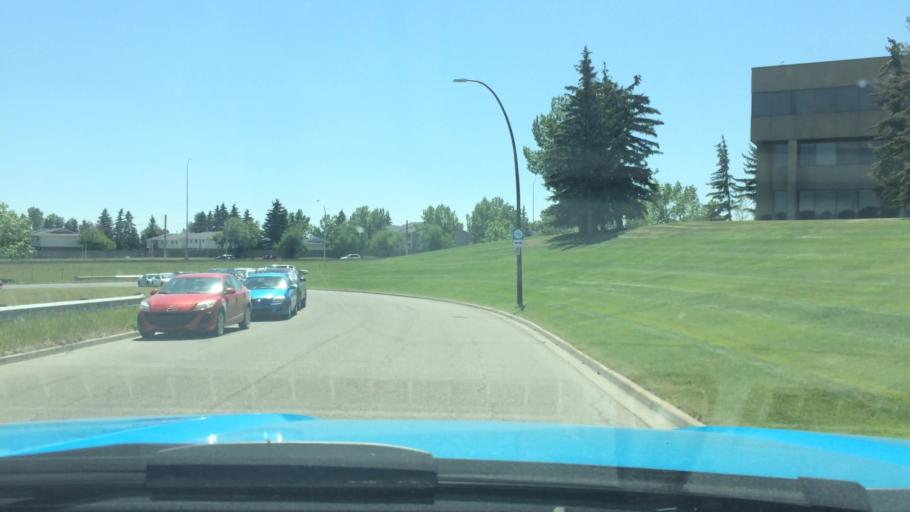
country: CA
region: Alberta
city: Calgary
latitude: 51.0517
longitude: -113.9894
